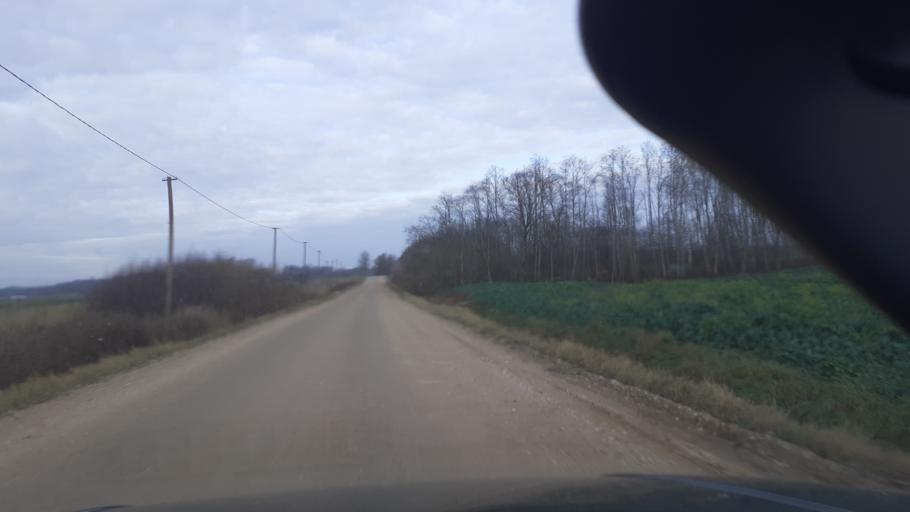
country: LV
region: Alsunga
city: Alsunga
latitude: 56.9046
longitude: 21.6547
